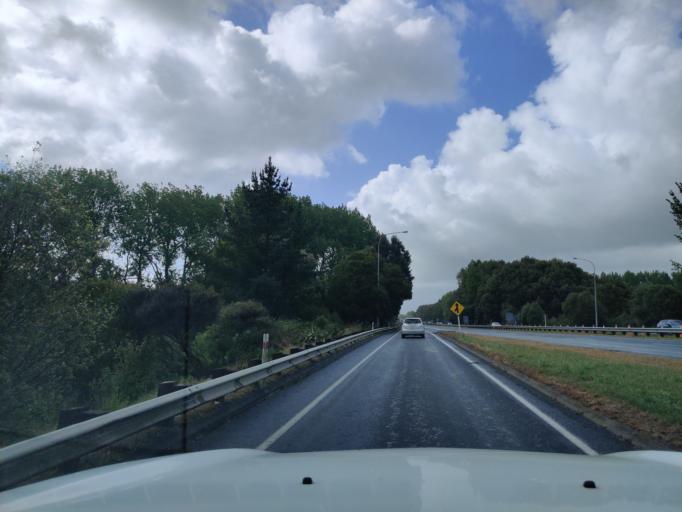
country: NZ
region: Waikato
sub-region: Hamilton City
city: Hamilton
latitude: -37.8296
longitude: 175.3591
